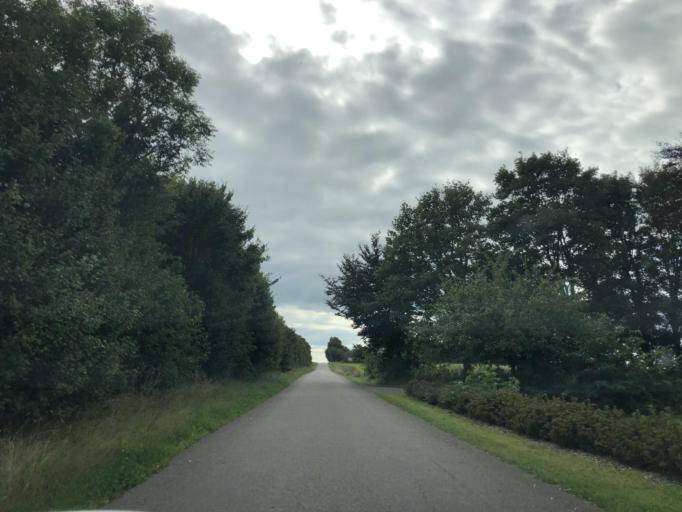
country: DK
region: North Denmark
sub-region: Vesthimmerland Kommune
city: Aars
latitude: 56.8313
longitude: 9.6598
